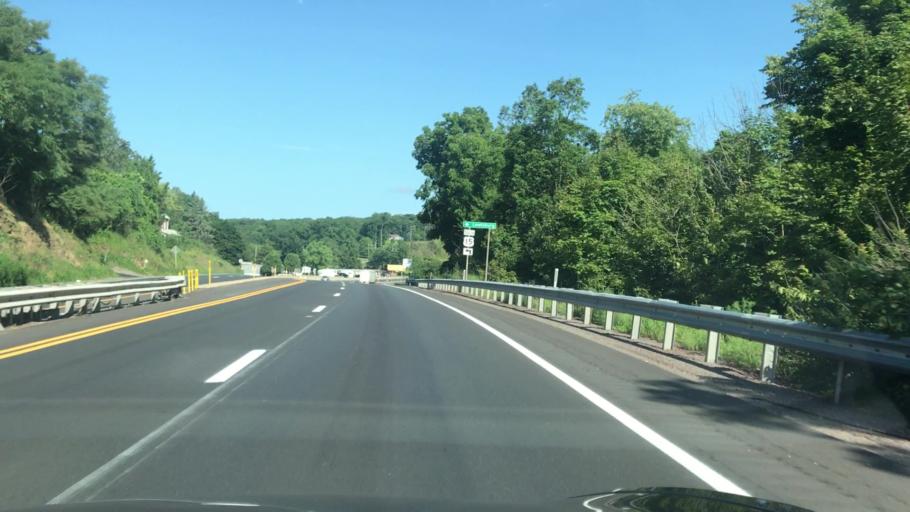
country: US
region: Pennsylvania
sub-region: Northumberland County
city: Watsontown
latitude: 41.0905
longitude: -76.8812
